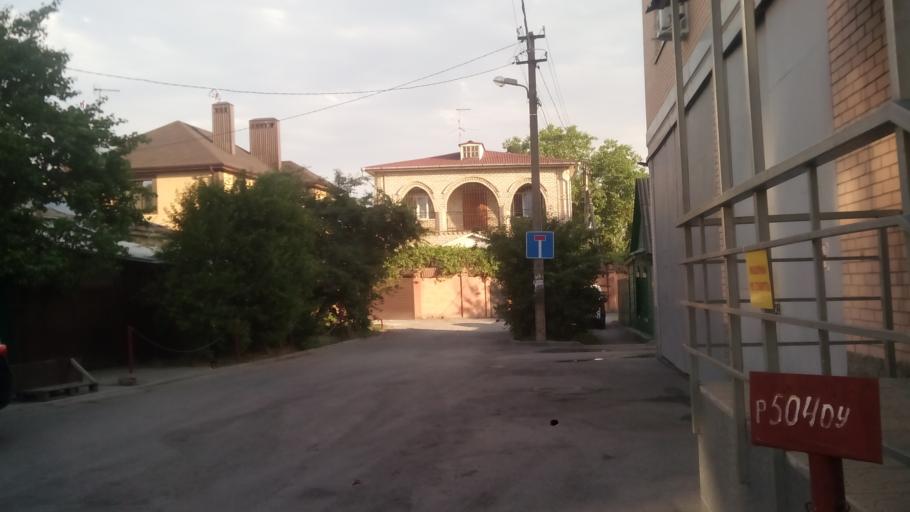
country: RU
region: Rostov
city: Imeni Chkalova
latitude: 47.2487
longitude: 39.7521
